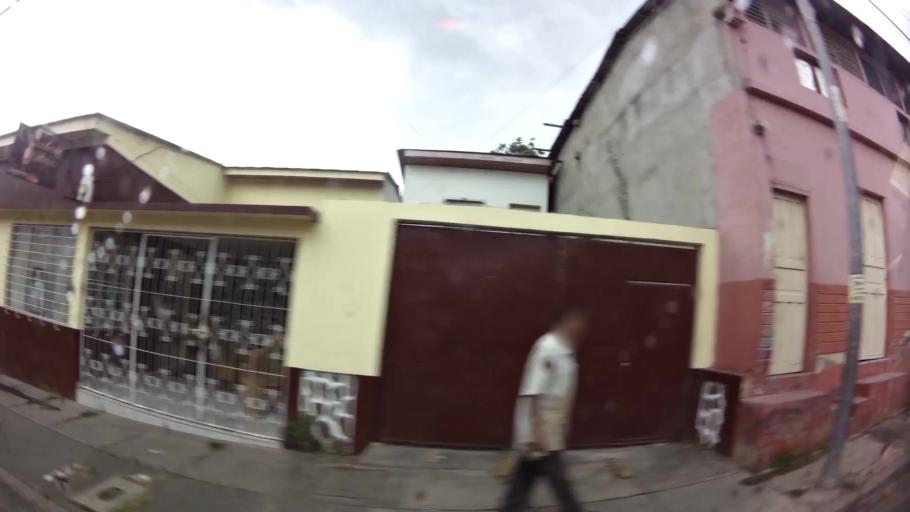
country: NI
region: Jinotega
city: Jinotega
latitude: 13.0909
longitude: -86.0010
